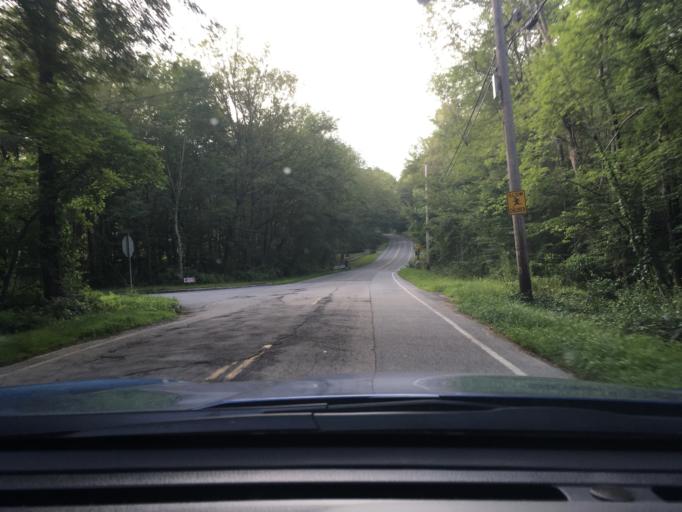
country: US
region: Rhode Island
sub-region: Washington County
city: Exeter
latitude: 41.6311
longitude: -71.5138
